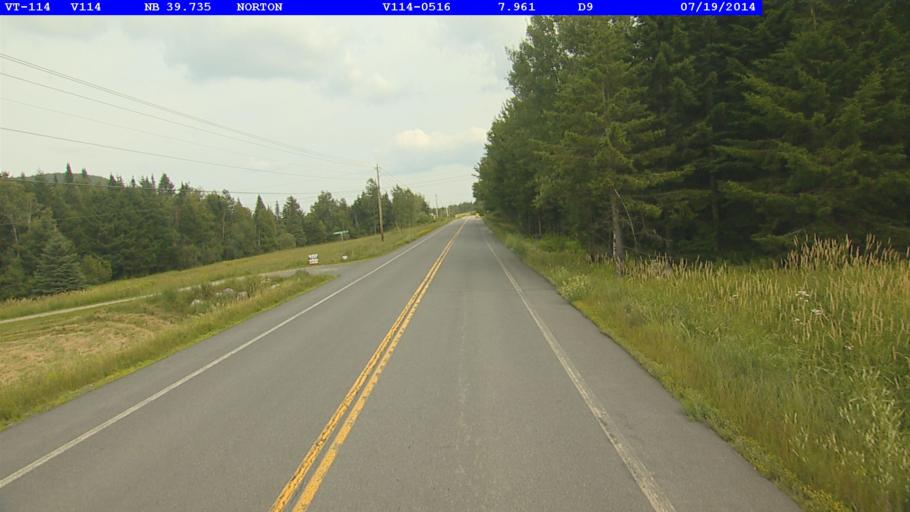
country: CA
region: Quebec
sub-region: Estrie
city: Coaticook
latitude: 44.9981
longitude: -71.7460
